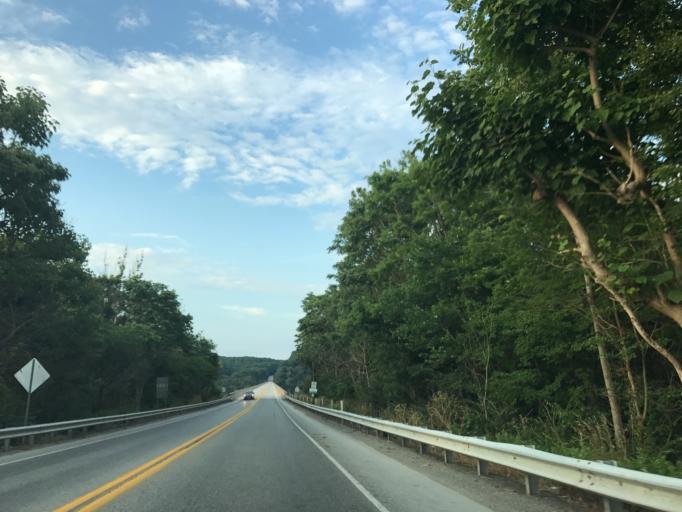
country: US
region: Pennsylvania
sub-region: York County
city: Susquehanna Trails
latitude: 39.8129
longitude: -76.3277
